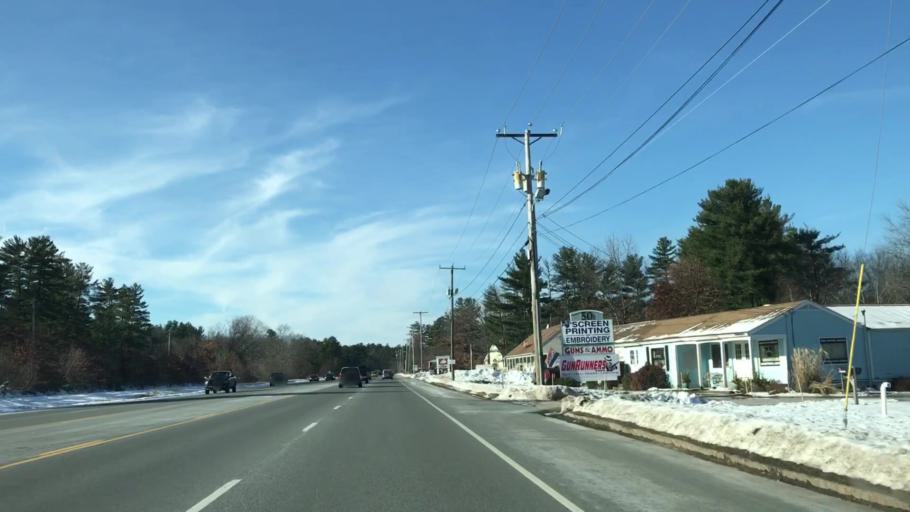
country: US
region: New Hampshire
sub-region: Hillsborough County
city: Milford
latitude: 42.8128
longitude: -71.5932
